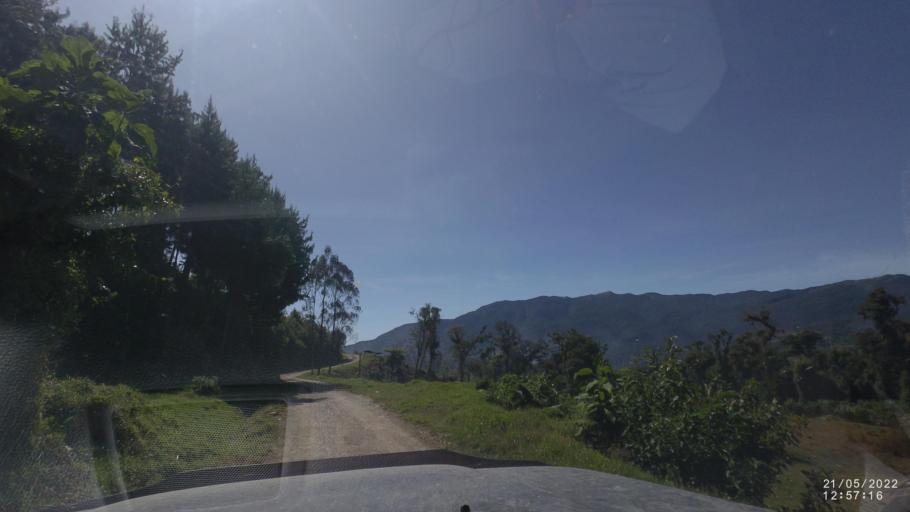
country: BO
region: Cochabamba
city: Colomi
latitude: -17.1704
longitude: -65.9455
